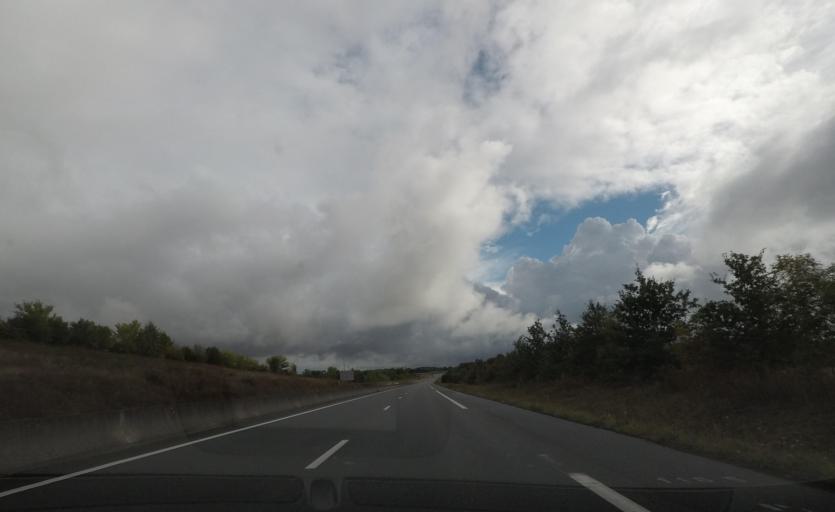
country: FR
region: Pays de la Loire
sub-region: Departement de la Vendee
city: La Roche-sur-Yon
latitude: 46.6484
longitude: -1.3896
